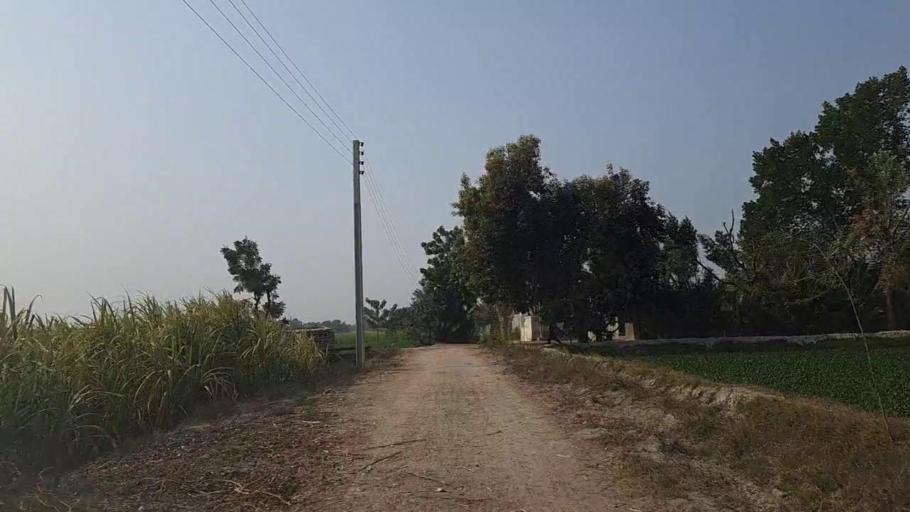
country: PK
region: Sindh
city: Daur
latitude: 26.4779
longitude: 68.4818
